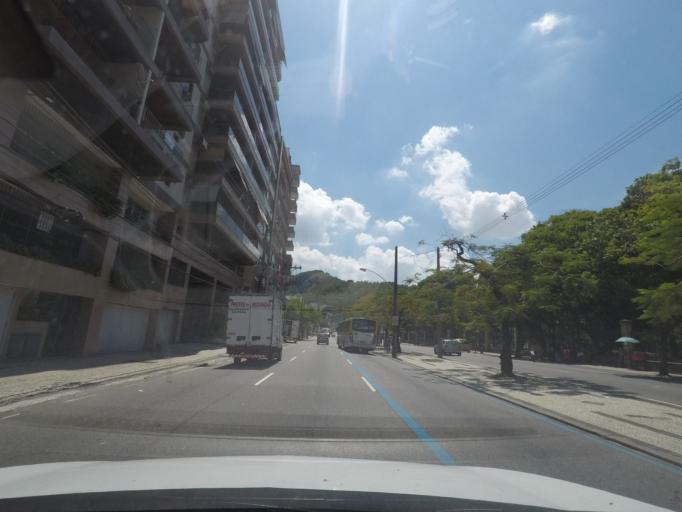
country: BR
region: Rio de Janeiro
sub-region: Rio De Janeiro
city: Rio de Janeiro
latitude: -22.9169
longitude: -43.2604
